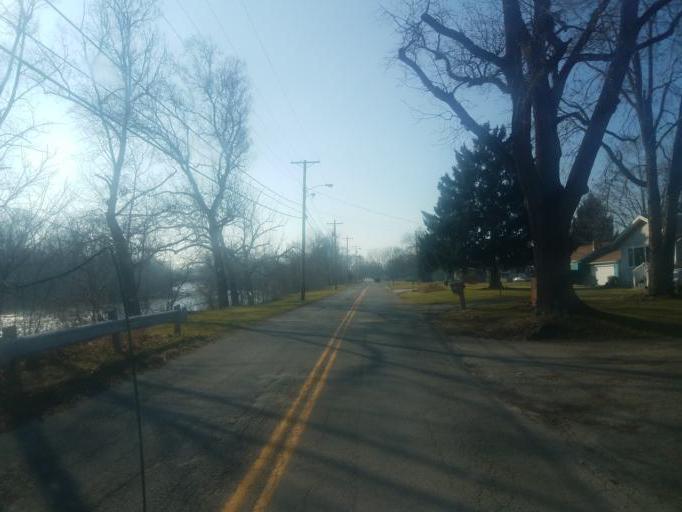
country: US
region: Ohio
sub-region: Seneca County
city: Tiffin
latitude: 41.1332
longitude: -83.1651
